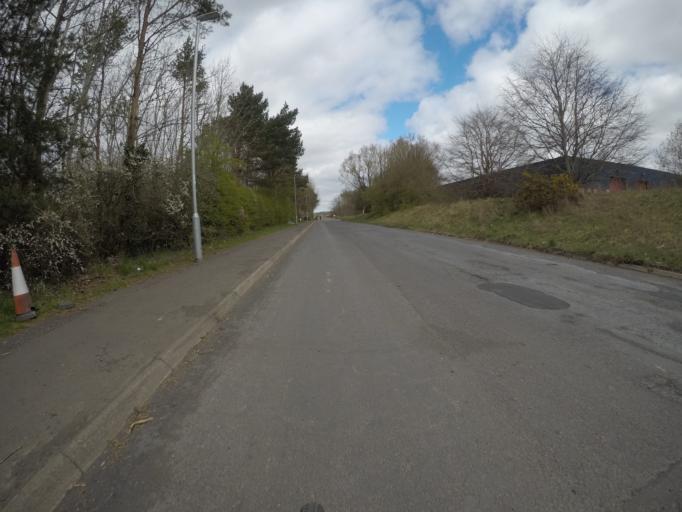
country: GB
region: Scotland
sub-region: North Ayrshire
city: Irvine
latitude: 55.6165
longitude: -4.6450
